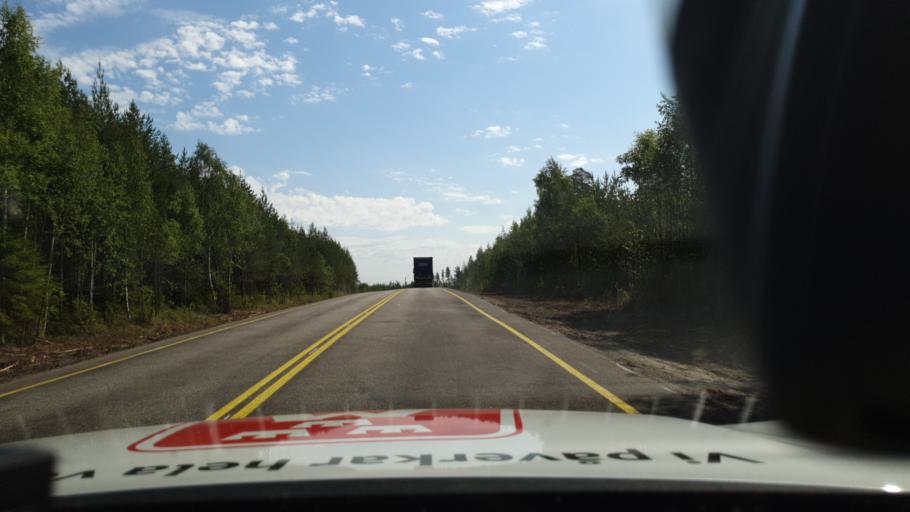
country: SE
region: Norrbotten
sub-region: Lulea Kommun
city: Ranea
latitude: 65.8717
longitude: 22.3542
